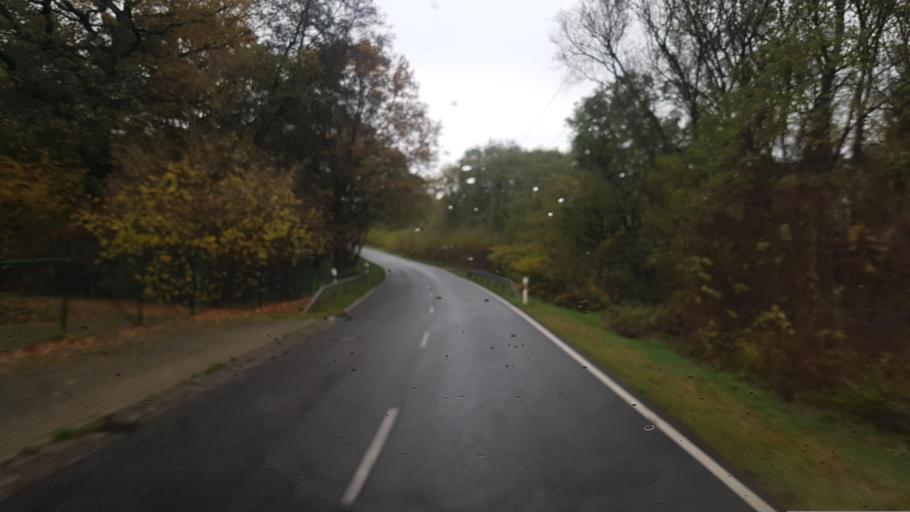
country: DE
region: Saxony-Anhalt
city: Abtsdorf
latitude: 51.8920
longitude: 12.7196
